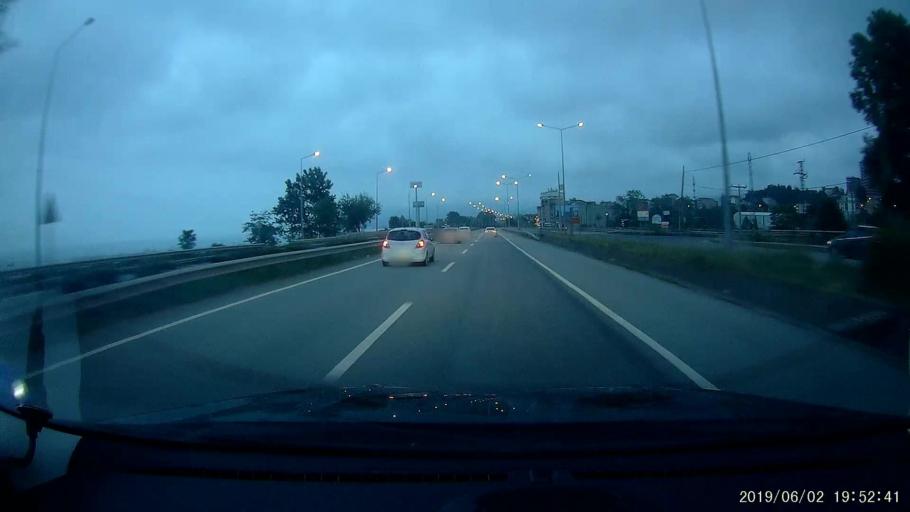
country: TR
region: Trabzon
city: Espiye
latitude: 40.9470
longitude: 38.6898
